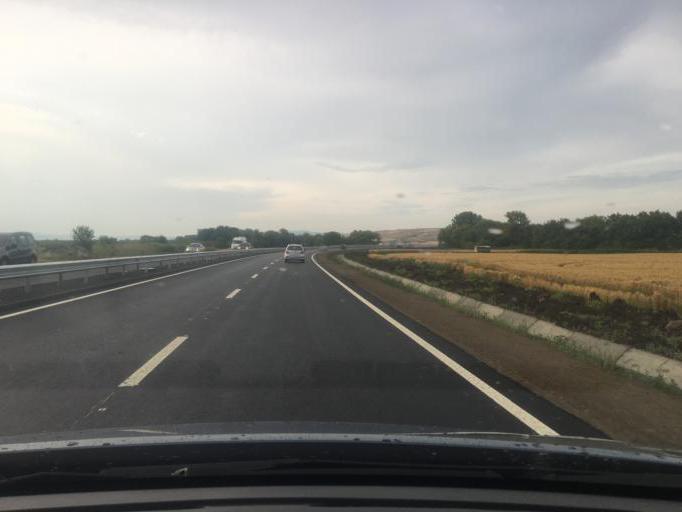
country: BG
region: Burgas
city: Aheloy
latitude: 42.6493
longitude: 27.6370
